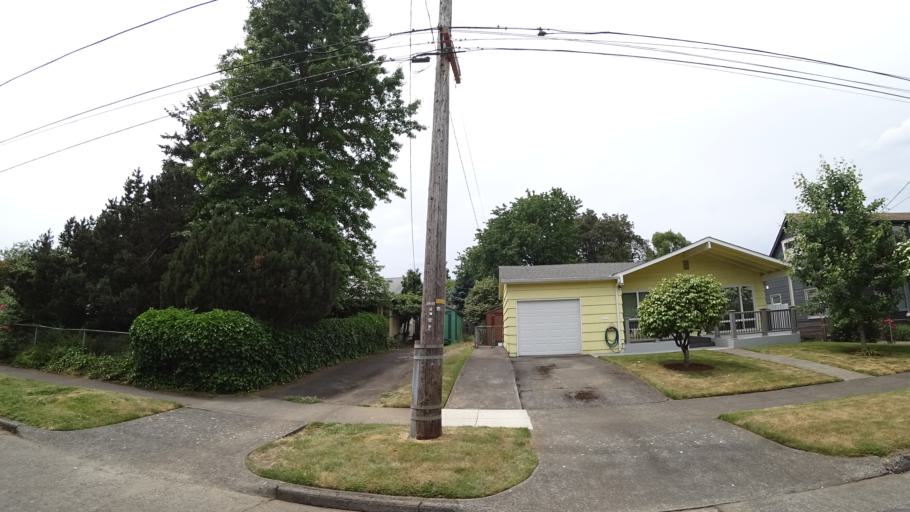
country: US
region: Oregon
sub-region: Multnomah County
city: Portland
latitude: 45.5652
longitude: -122.6892
